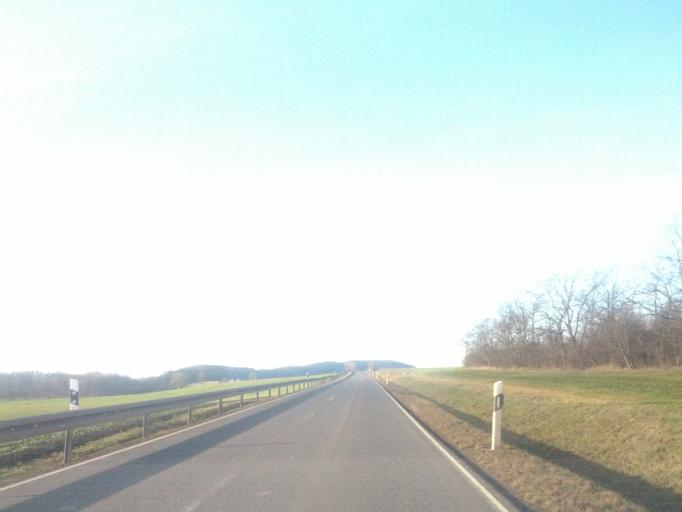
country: DE
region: Thuringia
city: Wandersleben
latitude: 50.9065
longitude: 10.8363
